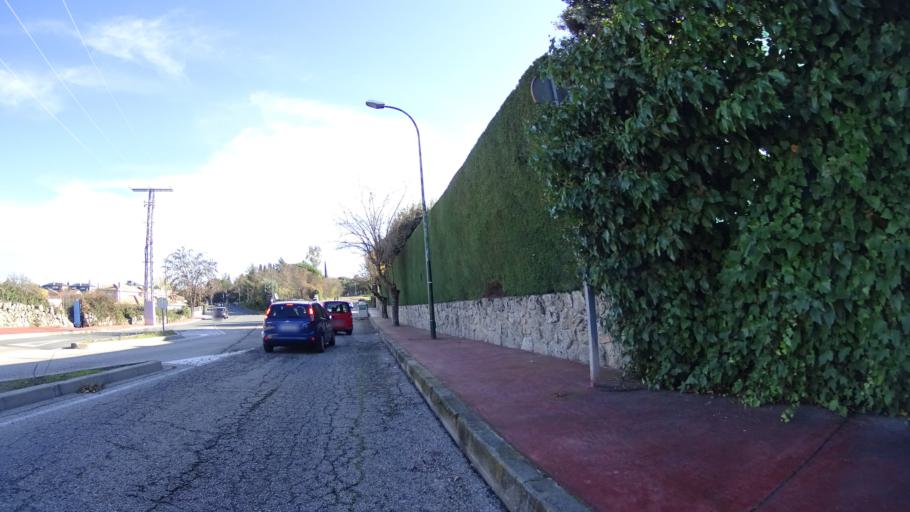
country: ES
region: Madrid
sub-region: Provincia de Madrid
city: Galapagar
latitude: 40.5721
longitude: -3.9919
